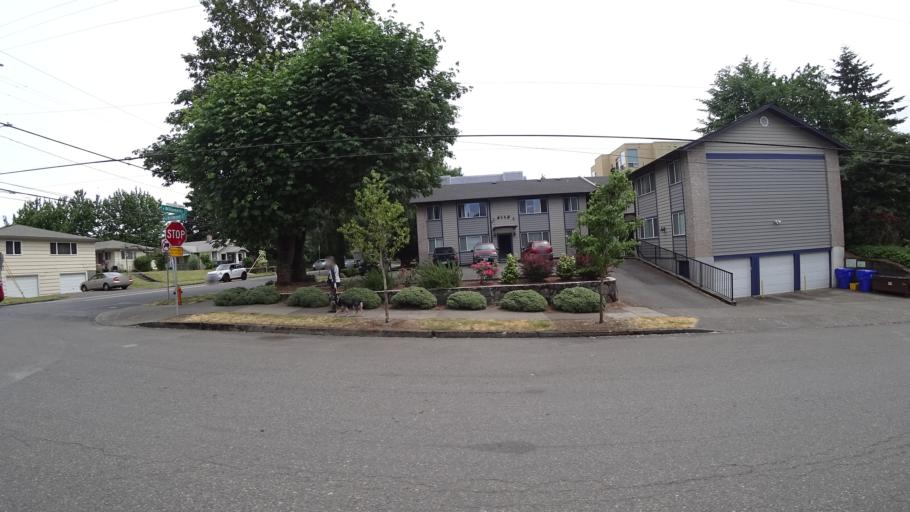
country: US
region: Oregon
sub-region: Washington County
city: West Haven
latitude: 45.5863
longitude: -122.7529
